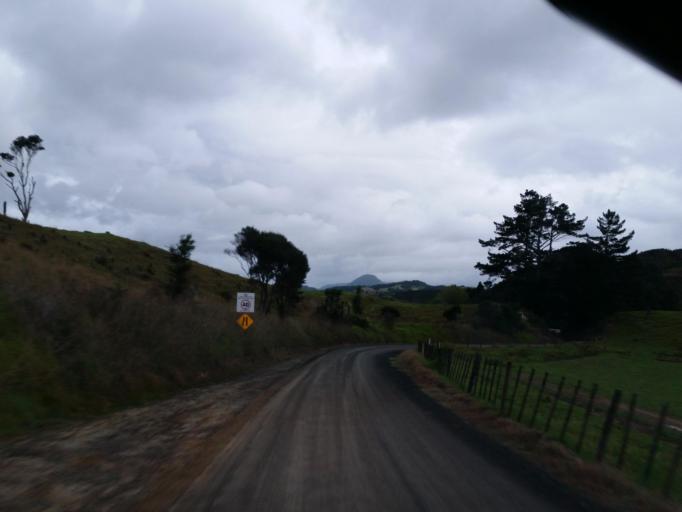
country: NZ
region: Northland
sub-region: Whangarei
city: Maungatapere
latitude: -35.8200
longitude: 174.0652
